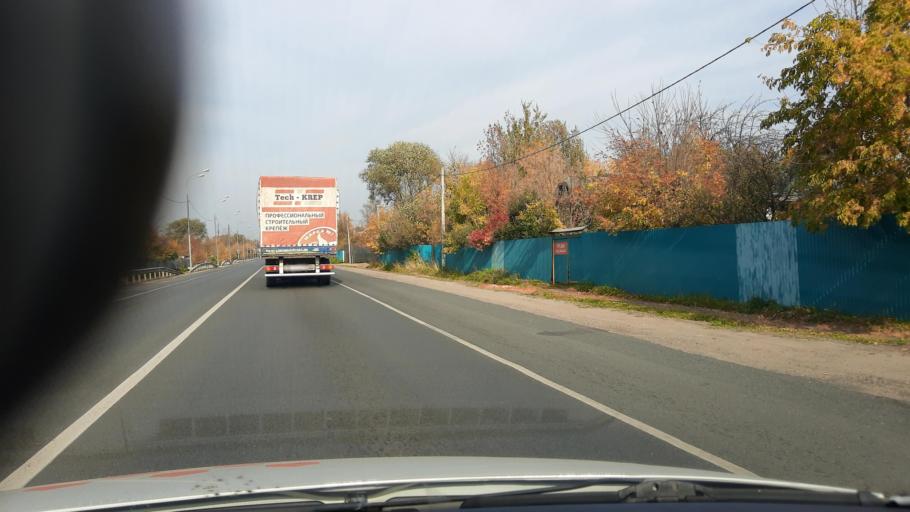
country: RU
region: Moskovskaya
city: Elektrostal'
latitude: 55.7832
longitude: 38.4321
